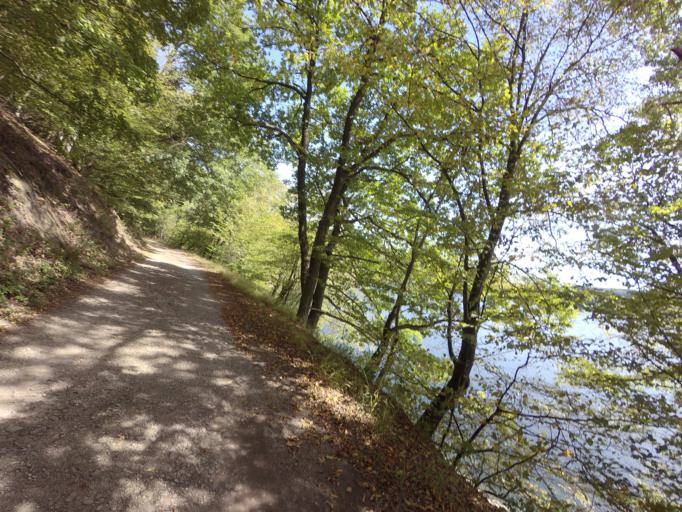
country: DE
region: North Rhine-Westphalia
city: Heimbach
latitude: 50.6425
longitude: 6.4065
